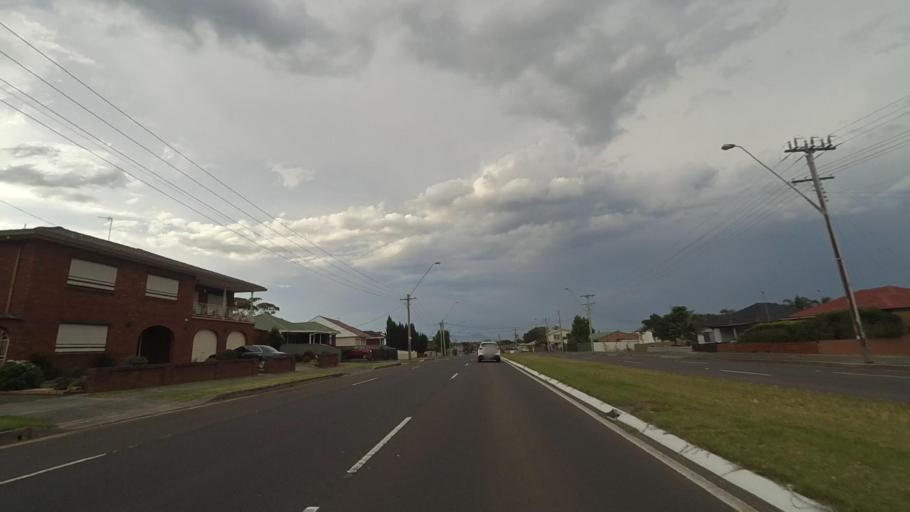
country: AU
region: New South Wales
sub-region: Shellharbour
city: Barrack Heights
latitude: -34.5631
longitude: 150.8601
